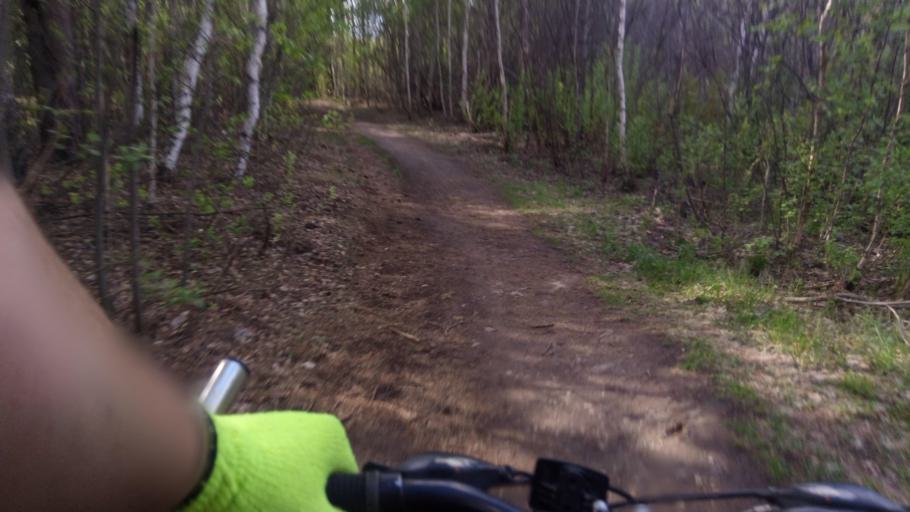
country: RU
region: Chelyabinsk
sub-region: Gorod Chelyabinsk
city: Chelyabinsk
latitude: 55.1680
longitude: 61.3306
